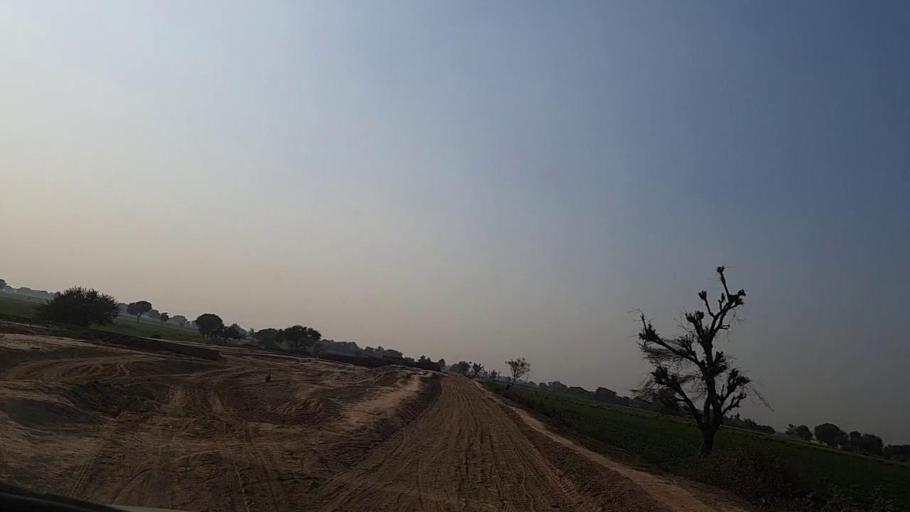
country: PK
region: Sindh
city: Sakrand
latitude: 26.0712
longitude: 68.2573
